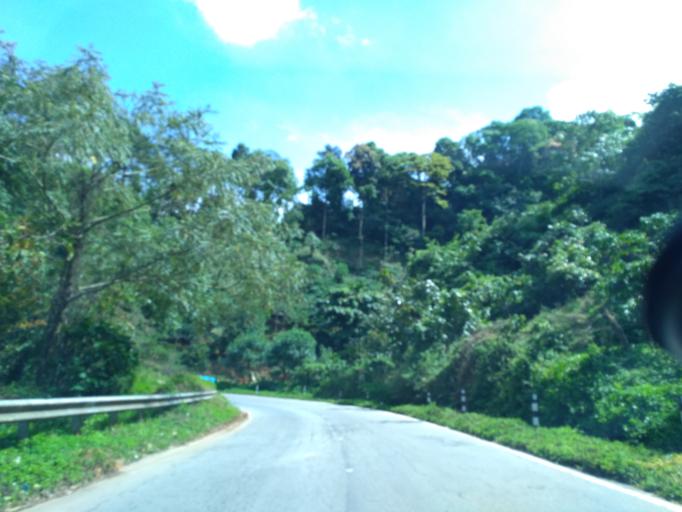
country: IN
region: Karnataka
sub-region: Kodagu
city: Madikeri
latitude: 12.4331
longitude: 75.6714
